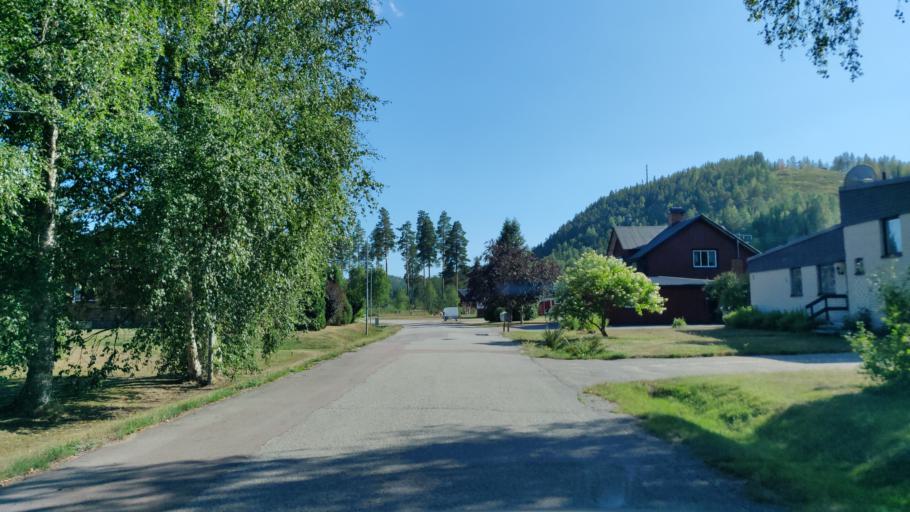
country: SE
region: Vaermland
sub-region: Hagfors Kommun
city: Ekshaerad
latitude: 60.1712
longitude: 13.4925
